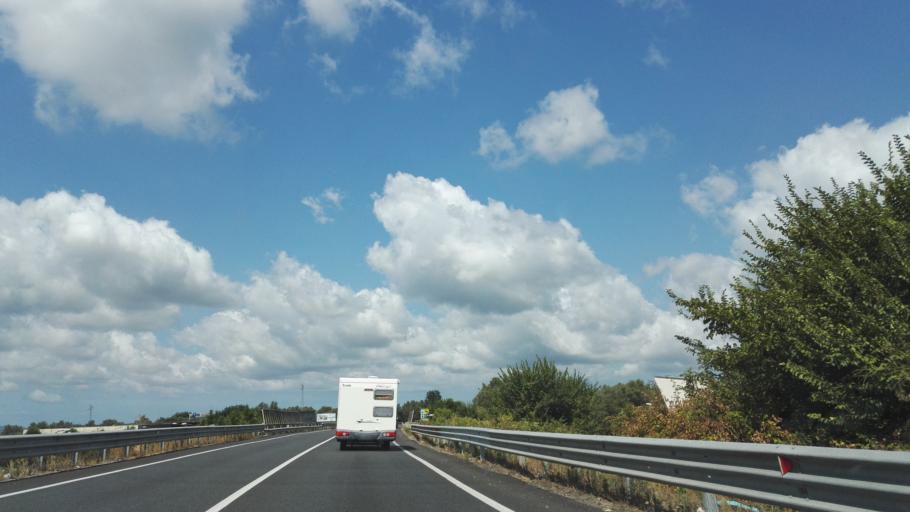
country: IT
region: Calabria
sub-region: Provincia di Reggio Calabria
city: Polistena
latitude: 38.4178
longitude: 16.0717
